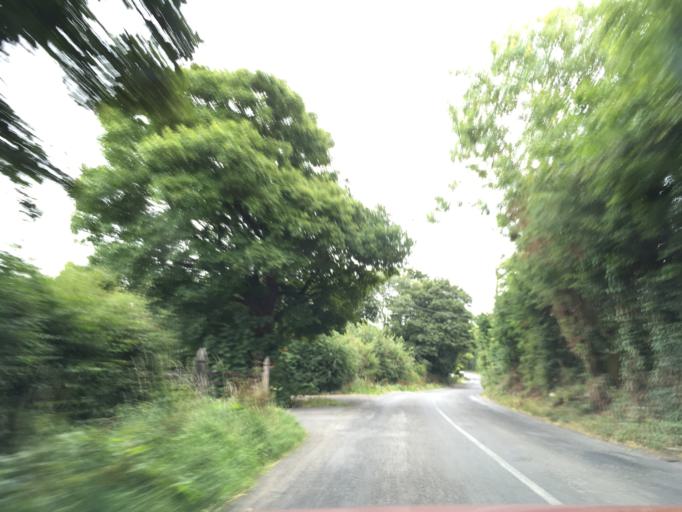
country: IE
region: Munster
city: Cashel
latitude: 52.4685
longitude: -7.8489
